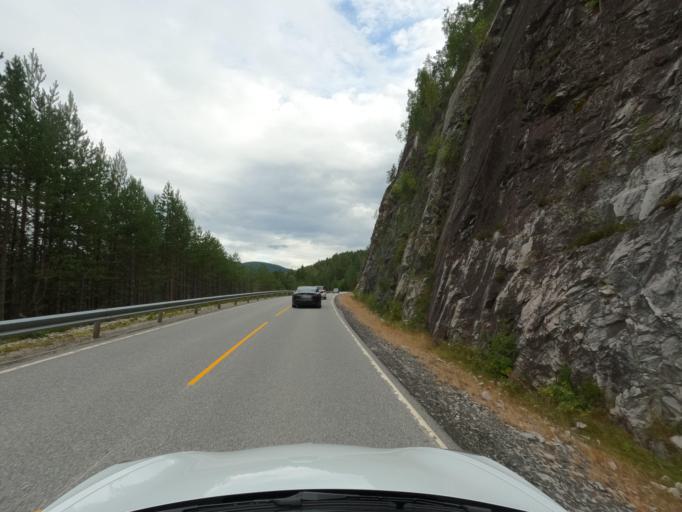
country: NO
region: Telemark
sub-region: Hjartdal
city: Sauland
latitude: 59.7752
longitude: 9.0102
